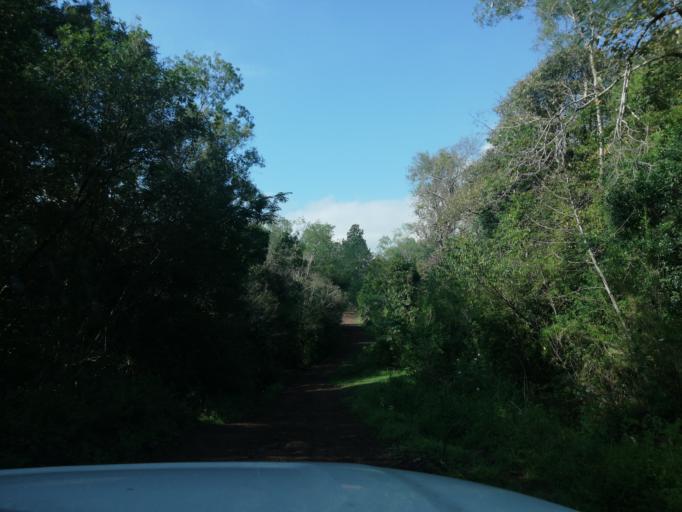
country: AR
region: Misiones
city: Cerro Azul
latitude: -27.5877
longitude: -55.5146
